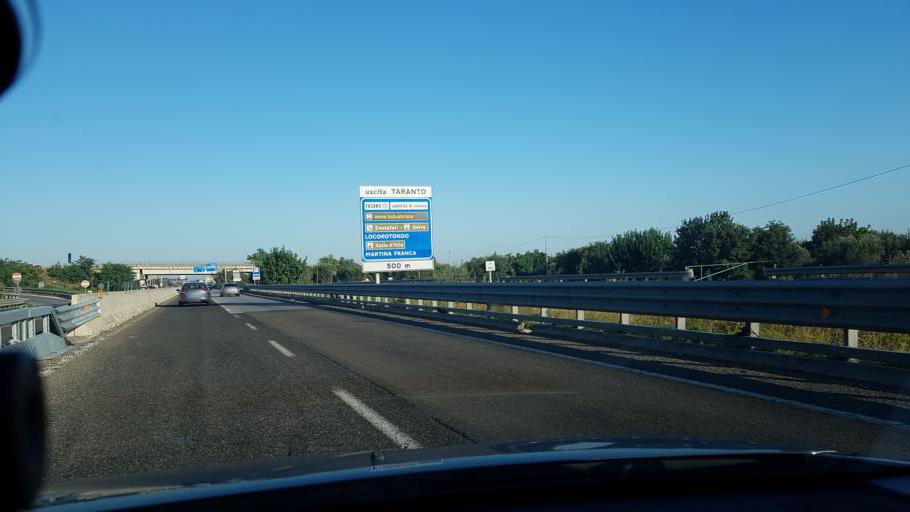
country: IT
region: Apulia
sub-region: Provincia di Brindisi
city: Fasano
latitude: 40.8488
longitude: 17.3597
